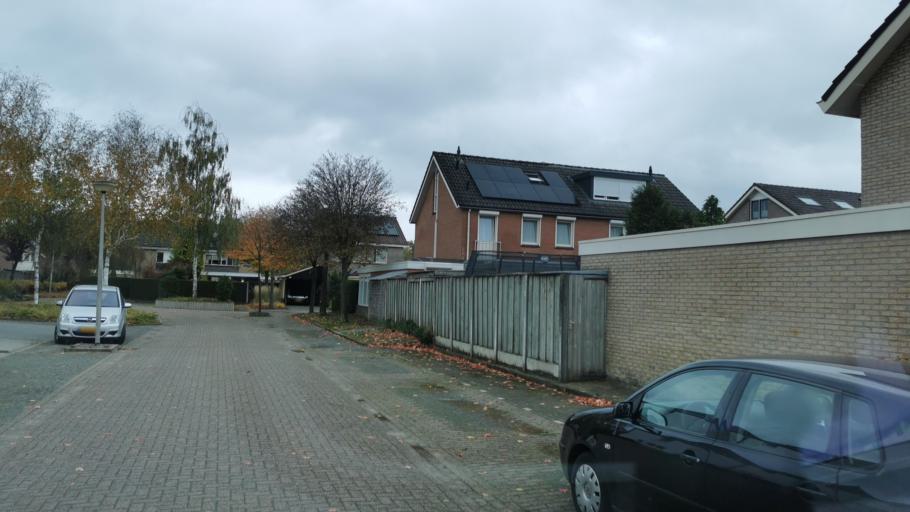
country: NL
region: Overijssel
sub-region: Gemeente Losser
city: Losser
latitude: 52.2563
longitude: 7.0005
